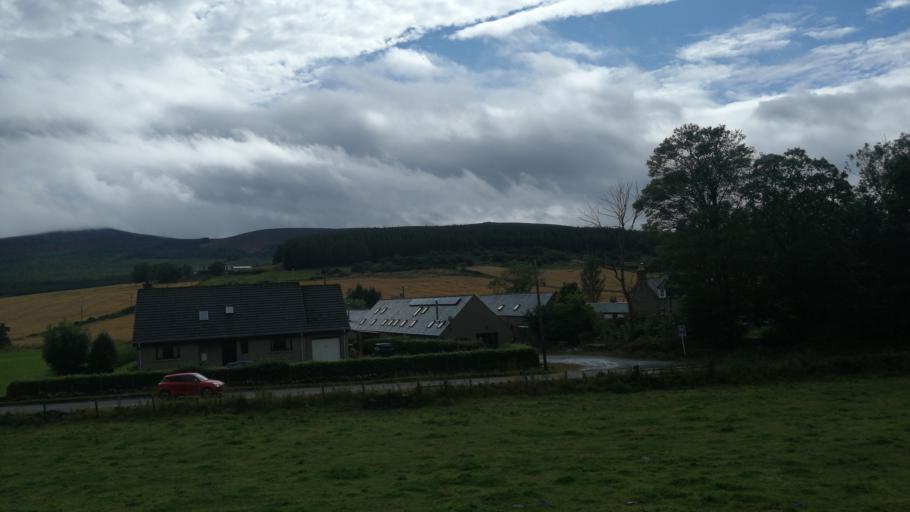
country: GB
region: Scotland
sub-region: Aberdeenshire
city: Insch
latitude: 57.3250
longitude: -2.5718
